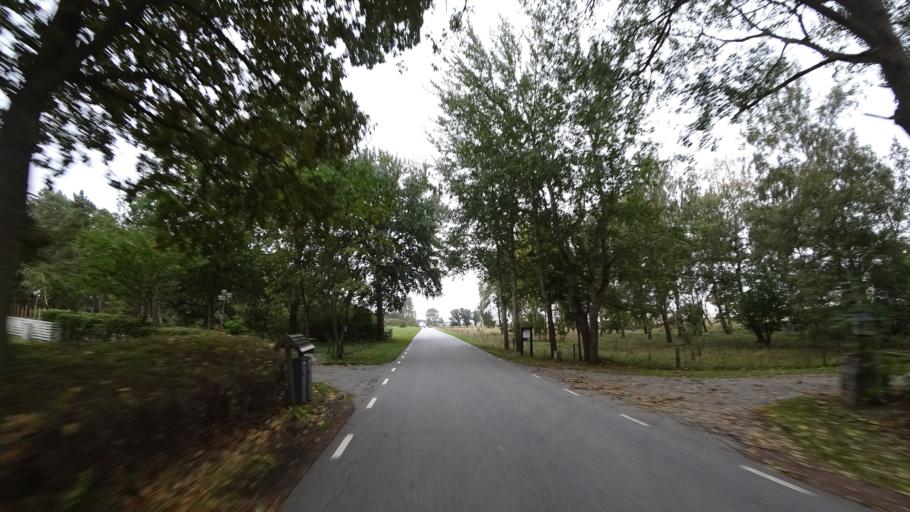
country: SE
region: Skane
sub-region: Kavlinge Kommun
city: Hofterup
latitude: 55.8188
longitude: 12.9327
